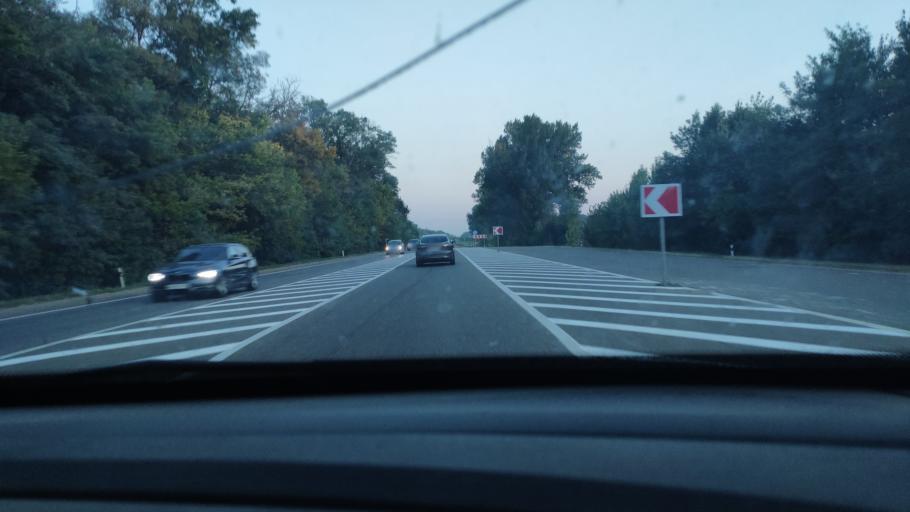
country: RU
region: Krasnodarskiy
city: Medvedovskaya
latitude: 45.4603
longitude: 38.9859
